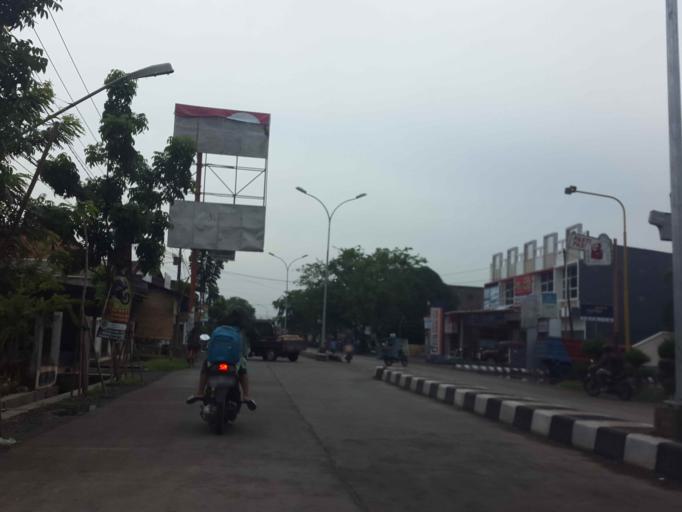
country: ID
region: Central Java
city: Semarang
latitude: -6.9612
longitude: 110.4788
